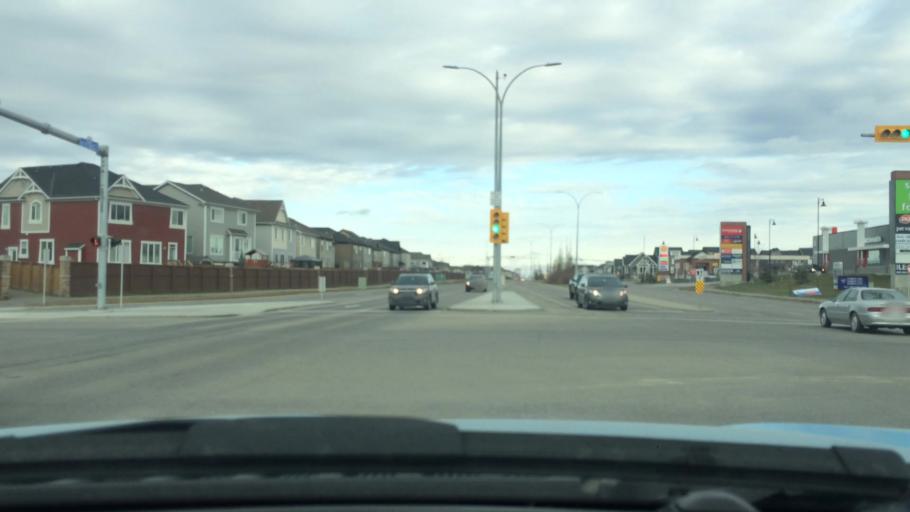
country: CA
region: Alberta
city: Airdrie
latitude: 51.2561
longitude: -114.0250
